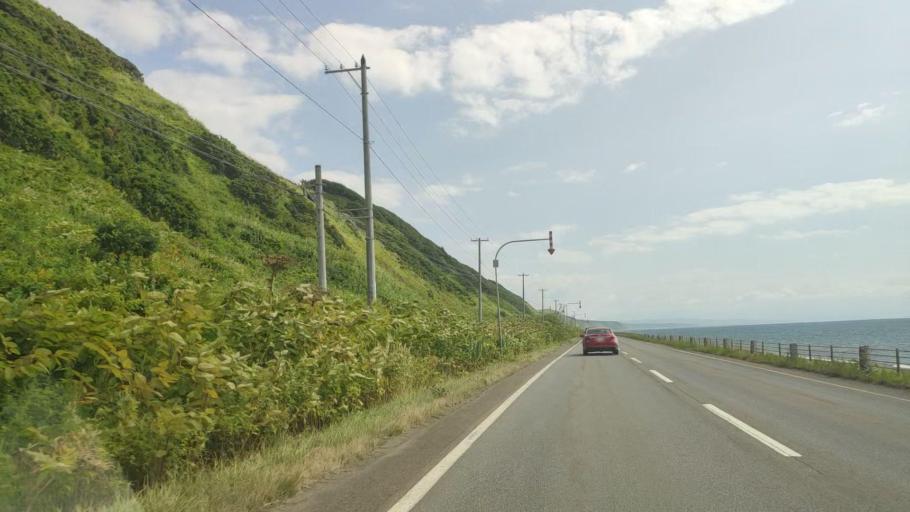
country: JP
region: Hokkaido
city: Rumoi
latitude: 44.0847
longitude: 141.6620
